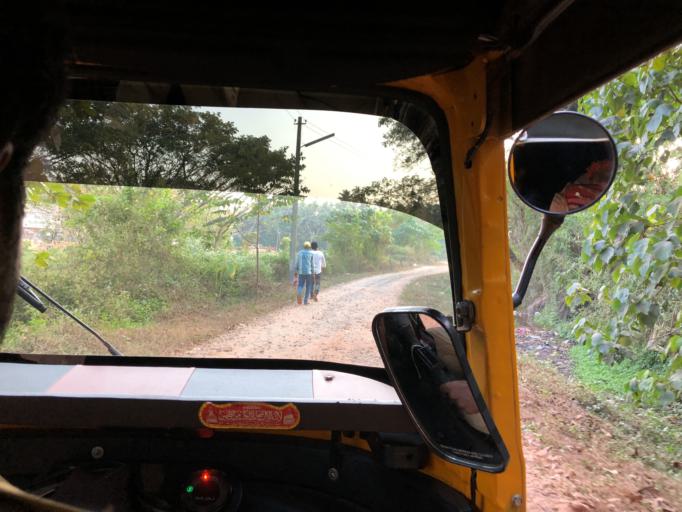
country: IN
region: Karnataka
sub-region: Dakshina Kannada
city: Mangalore
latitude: 12.8990
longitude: 74.8660
